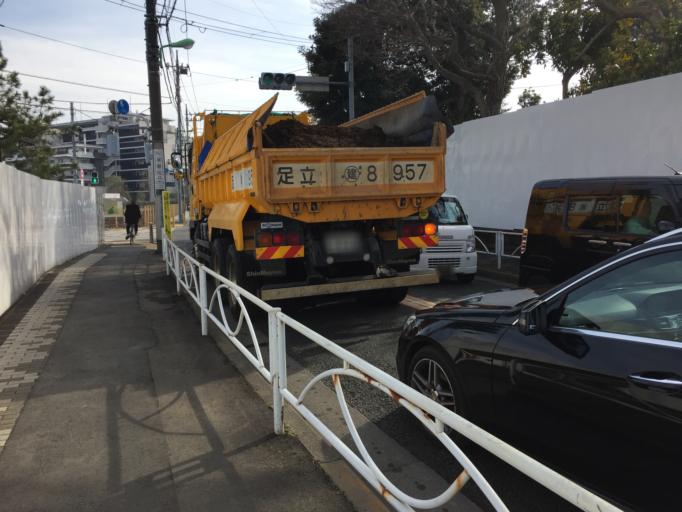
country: JP
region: Tokyo
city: Tokyo
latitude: 35.6367
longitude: 139.6361
